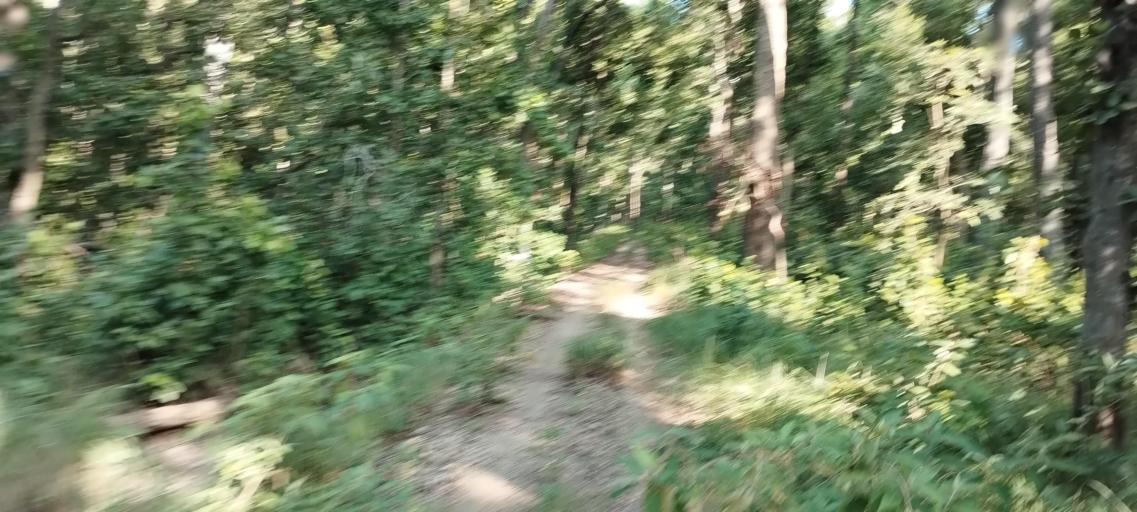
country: NP
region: Far Western
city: Tikapur
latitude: 28.5231
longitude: 81.2623
